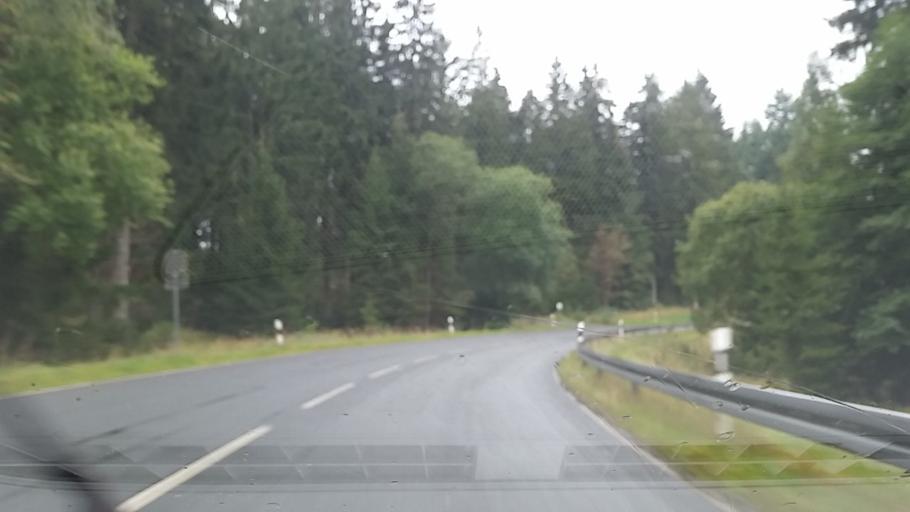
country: DE
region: Lower Saxony
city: Altenau
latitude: 51.7932
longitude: 10.4456
